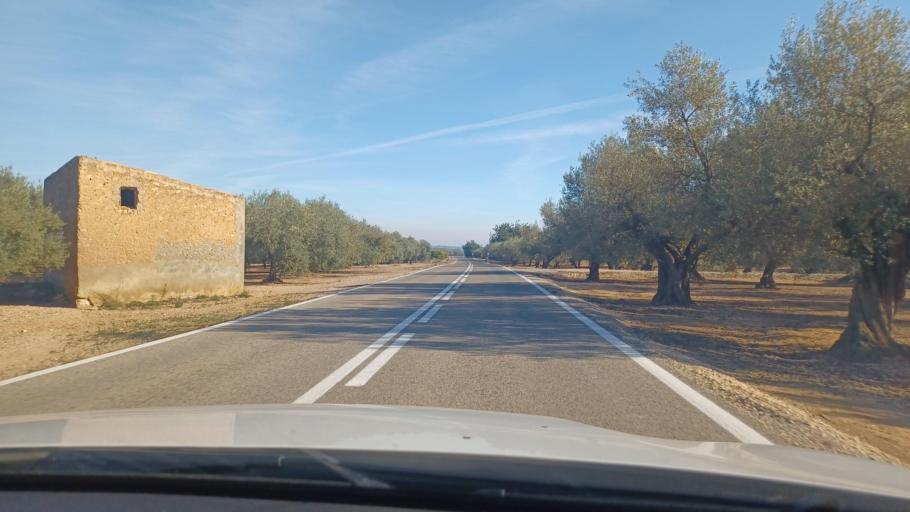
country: ES
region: Catalonia
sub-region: Provincia de Tarragona
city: Santa Barbara
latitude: 40.7197
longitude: 0.4569
